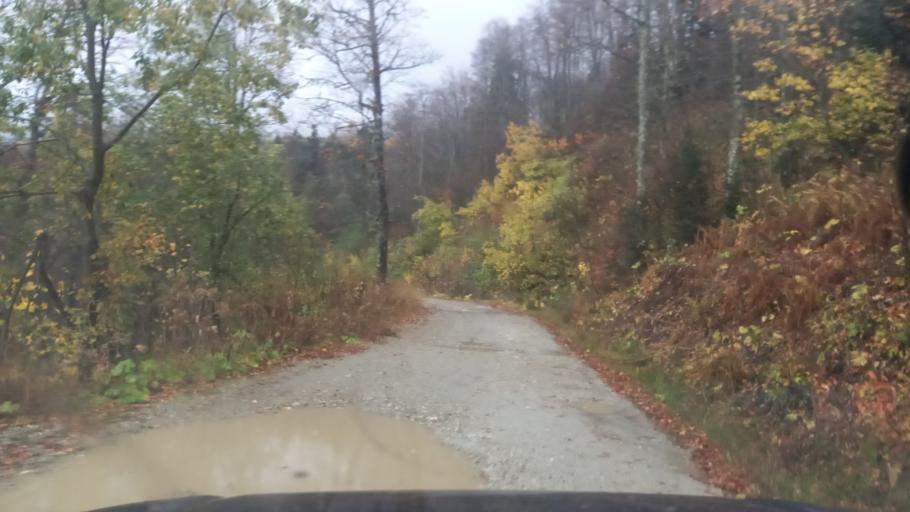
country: RU
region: Krasnodarskiy
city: Dagomys
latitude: 43.9919
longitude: 39.8540
